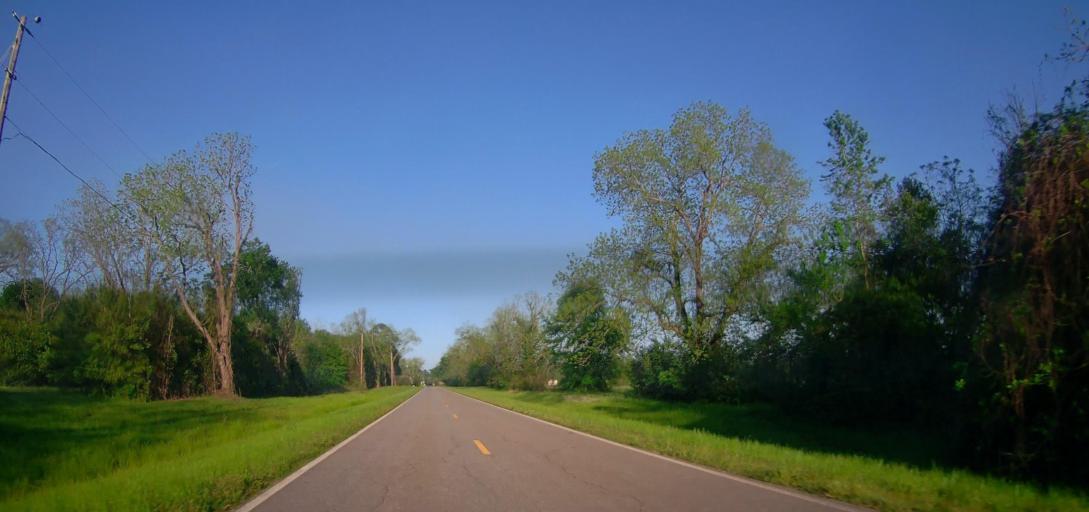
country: US
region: Georgia
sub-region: Macon County
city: Oglethorpe
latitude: 32.3016
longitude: -84.0758
